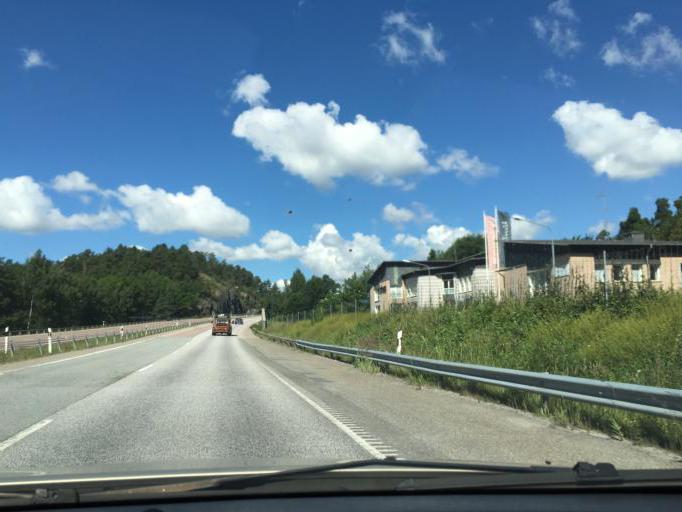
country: SE
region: Stockholm
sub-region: Nacka Kommun
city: Nacka
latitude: 59.3016
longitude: 18.1880
